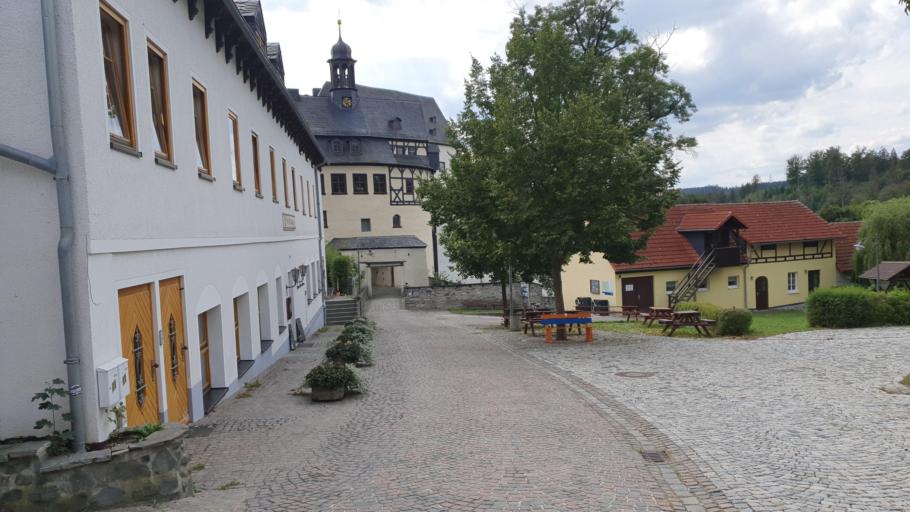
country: DE
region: Thuringia
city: Burgk
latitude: 50.5546
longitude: 11.7171
